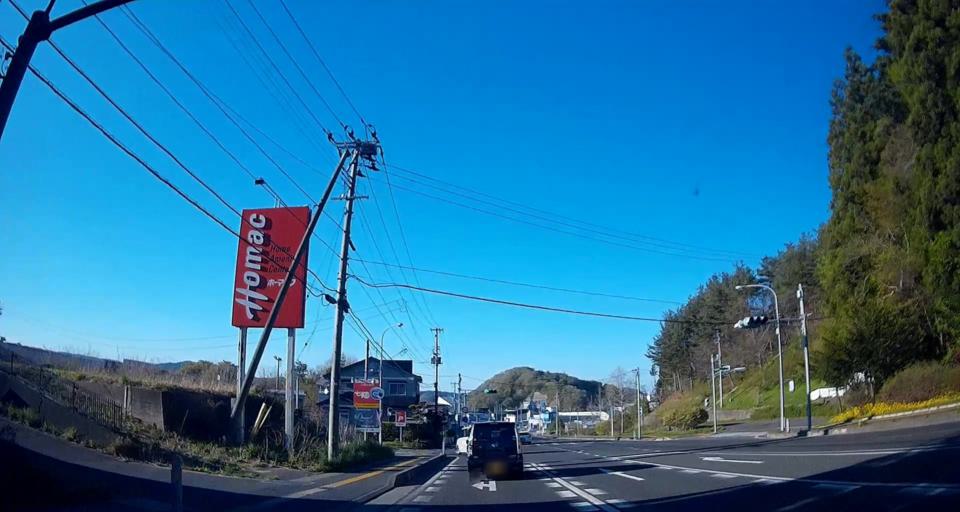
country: JP
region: Iwate
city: Miyako
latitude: 39.6188
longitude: 141.9615
